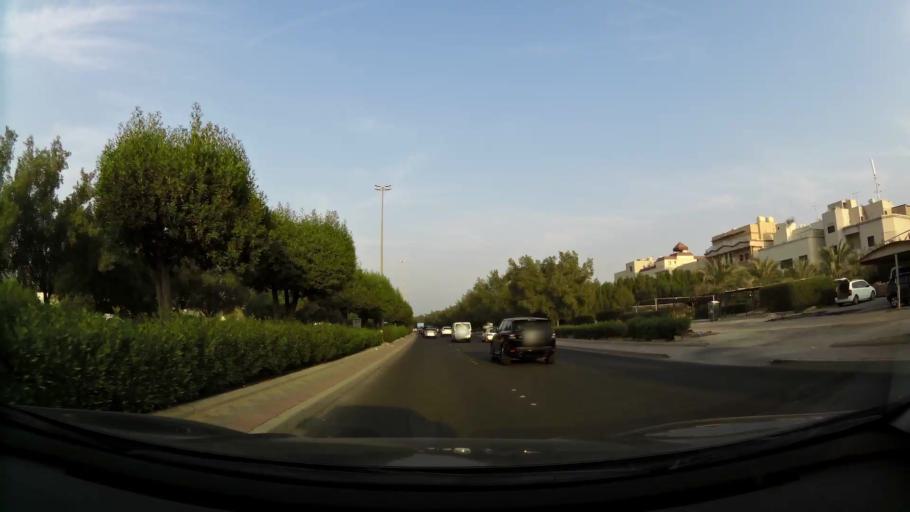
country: KW
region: Mubarak al Kabir
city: Sabah as Salim
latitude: 29.2436
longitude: 48.0764
